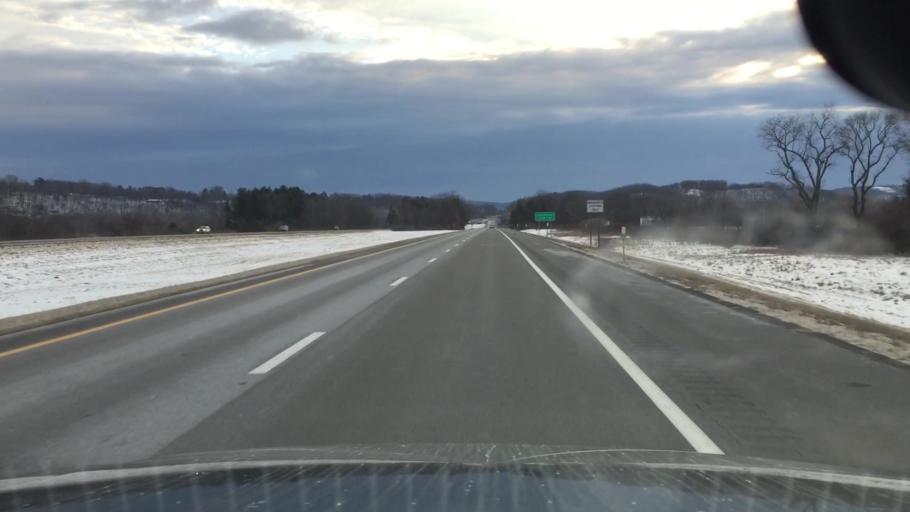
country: US
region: Pennsylvania
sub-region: Bradford County
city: South Waverly
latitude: 42.0006
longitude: -76.5752
